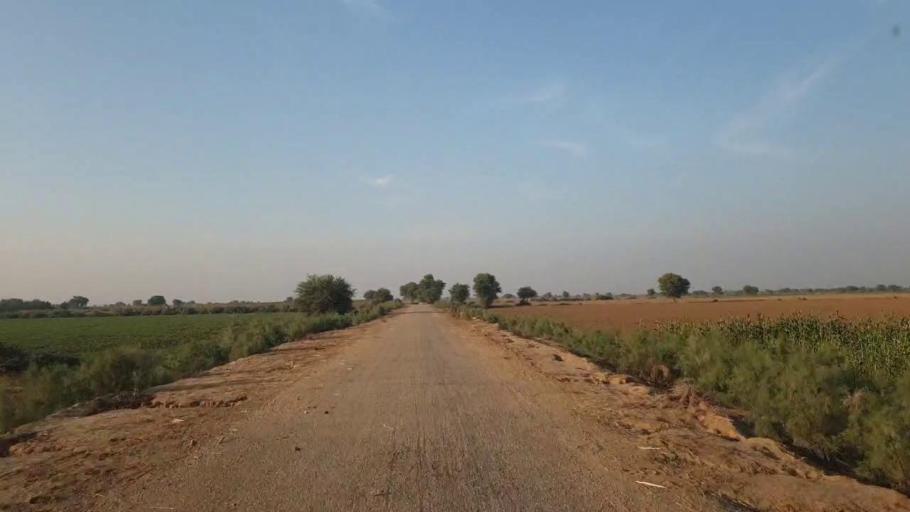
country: PK
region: Sindh
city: Sann
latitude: 25.9255
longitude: 68.1788
